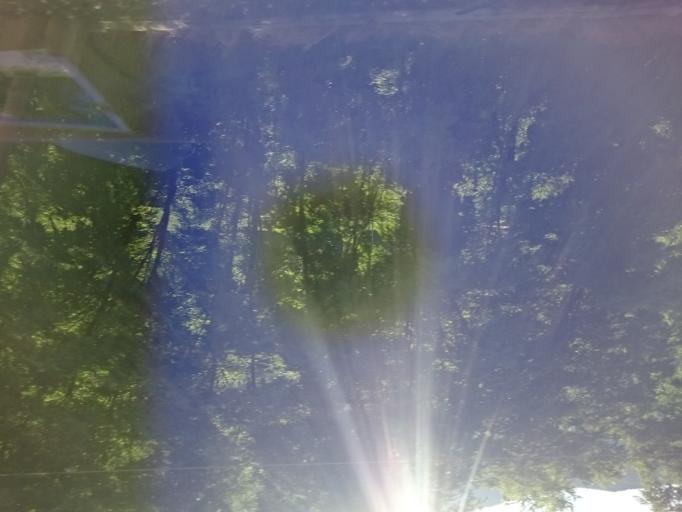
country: IT
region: Veneto
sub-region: Provincia di Verona
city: Dolce
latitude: 45.5936
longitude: 10.8480
